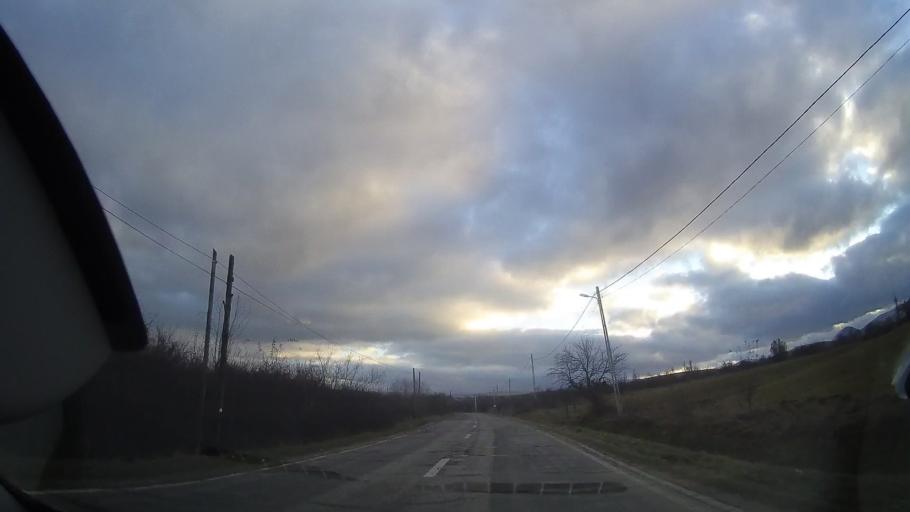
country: RO
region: Cluj
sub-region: Comuna Sancraiu
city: Sancraiu
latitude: 46.8101
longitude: 22.9935
